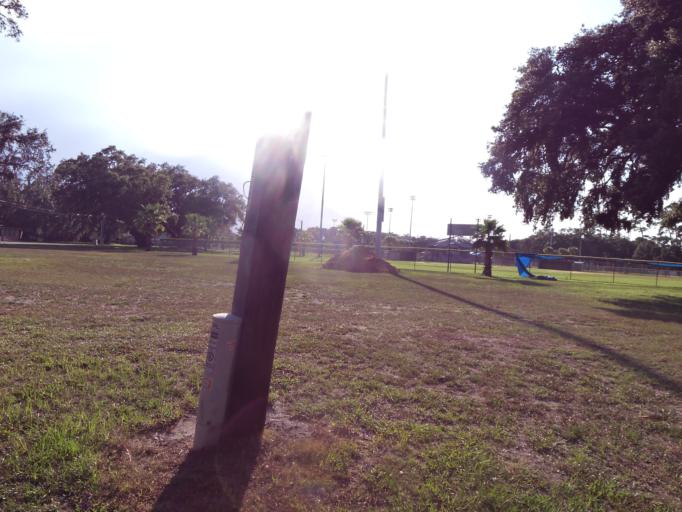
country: US
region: Florida
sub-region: Nassau County
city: Fernandina Beach
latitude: 30.6680
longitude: -81.4534
